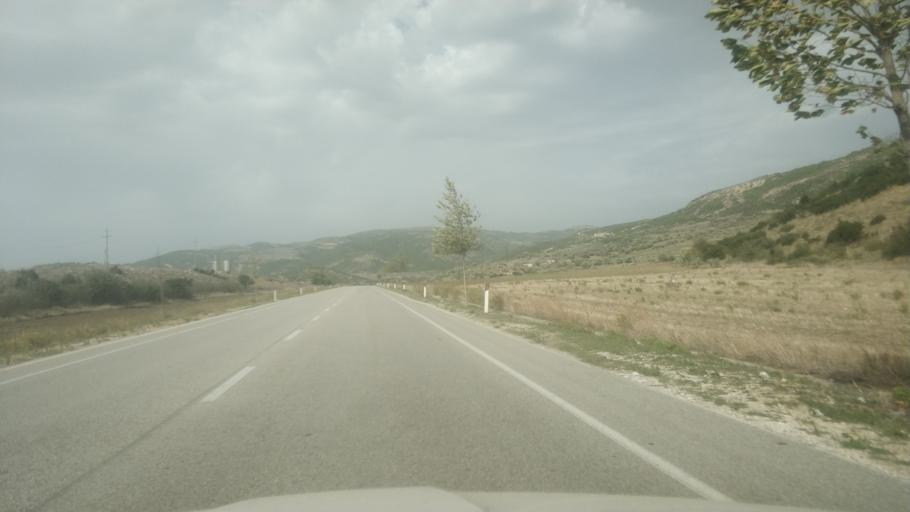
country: AL
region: Gjirokaster
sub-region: Rrethi i Tepelenes
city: Memaliaj
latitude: 40.3679
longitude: 19.9084
